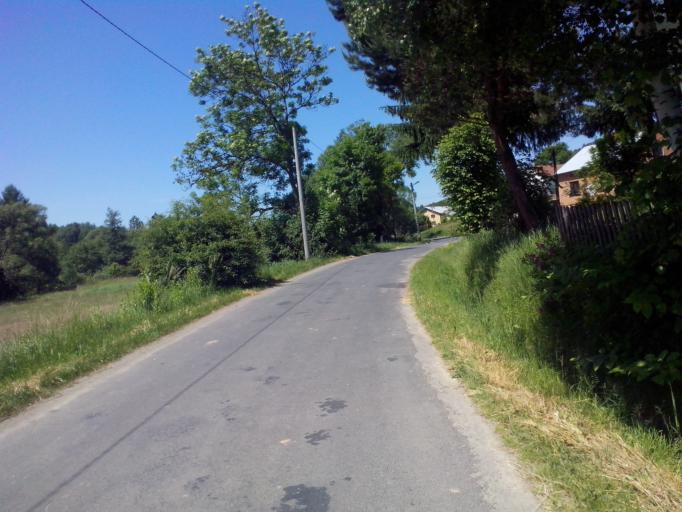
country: PL
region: Subcarpathian Voivodeship
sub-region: Powiat krosnienski
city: Wojaszowka
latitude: 49.8021
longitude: 21.6968
